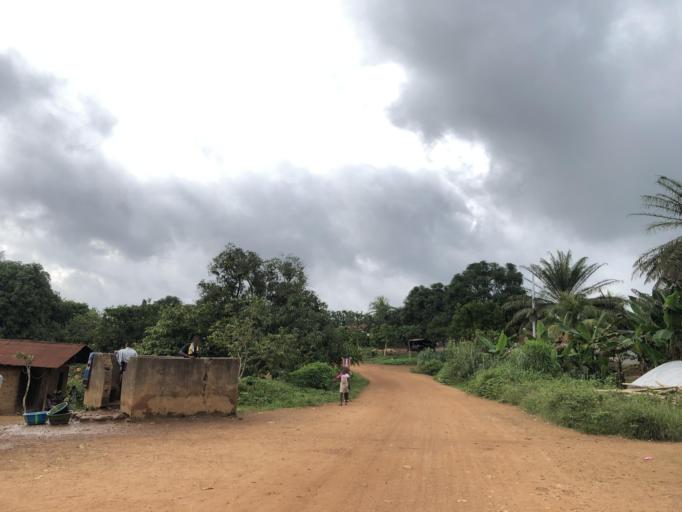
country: SL
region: Eastern Province
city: Kailahun
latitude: 8.2667
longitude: -10.5620
